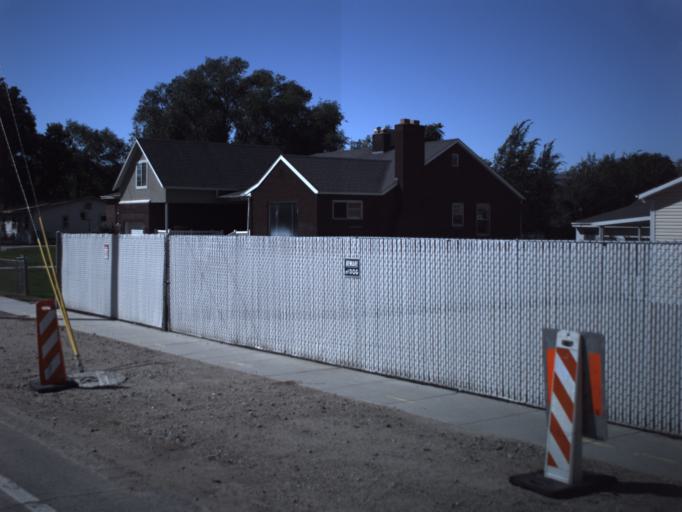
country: US
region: Utah
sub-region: Salt Lake County
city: Riverton
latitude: 40.5070
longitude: -111.9387
